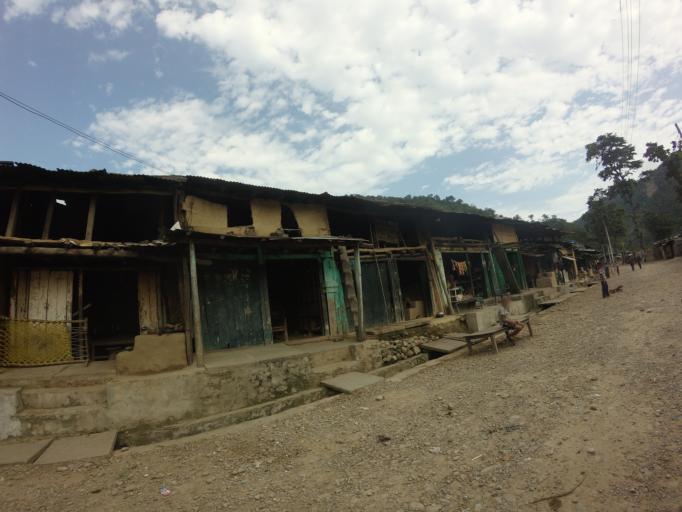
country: NP
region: Far Western
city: Tikapur
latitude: 28.6455
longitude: 81.2840
